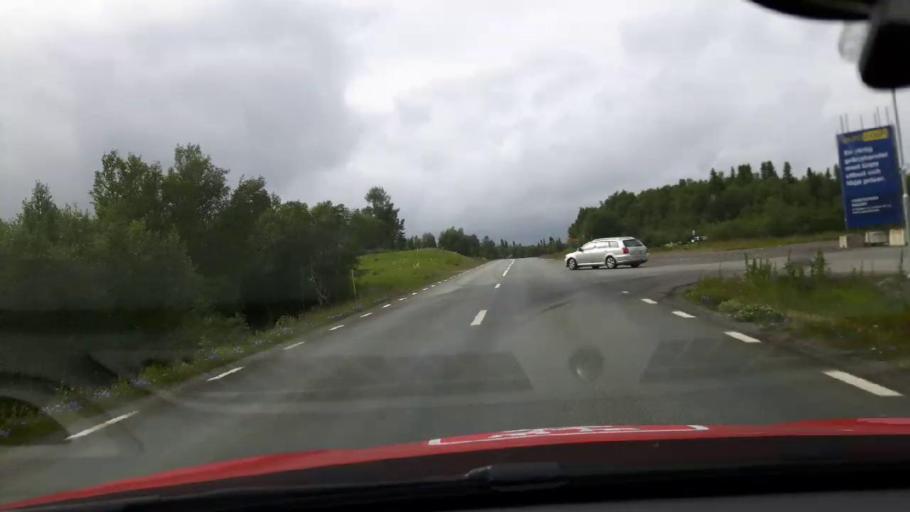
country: NO
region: Nord-Trondelag
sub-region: Meraker
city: Meraker
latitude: 63.2817
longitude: 12.1312
